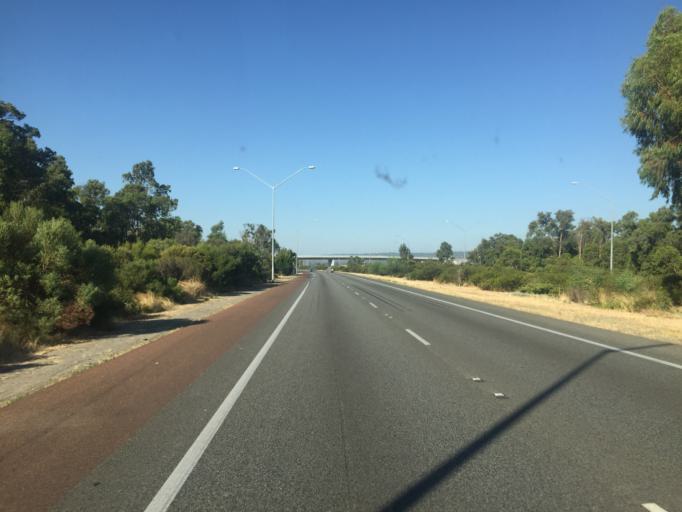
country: AU
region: Western Australia
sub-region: Gosnells
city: Kenwick
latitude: -32.0302
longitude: 115.9676
